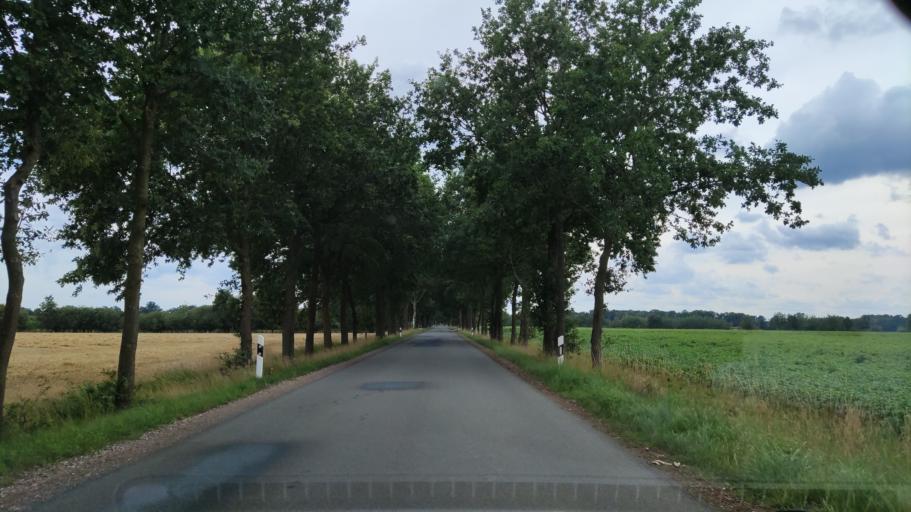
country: DE
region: Lower Saxony
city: Dannenberg
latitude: 53.0780
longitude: 11.1319
